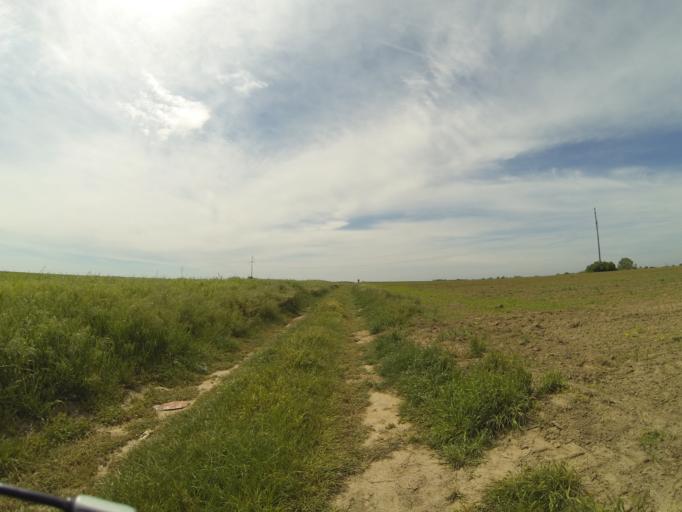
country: RO
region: Dolj
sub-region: Comuna Ghindeni
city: Ghindeni
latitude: 44.2154
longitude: 23.9390
